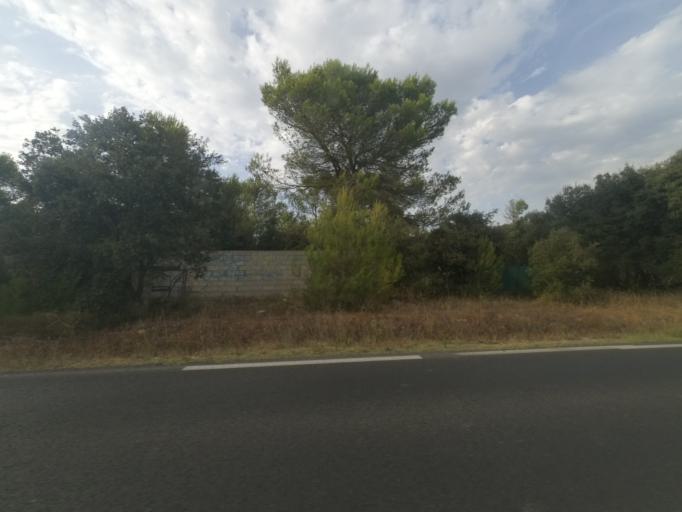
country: FR
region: Languedoc-Roussillon
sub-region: Departement de l'Herault
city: Sussargues
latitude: 43.6906
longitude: 4.0046
